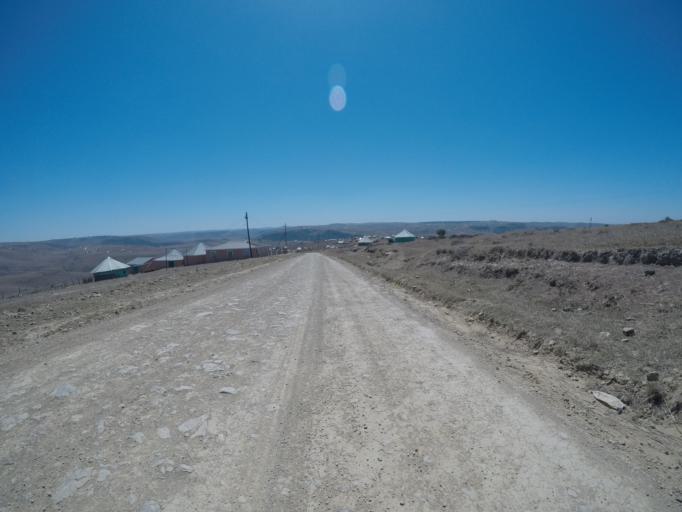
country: ZA
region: Eastern Cape
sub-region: OR Tambo District Municipality
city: Mthatha
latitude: -31.8879
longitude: 28.8762
